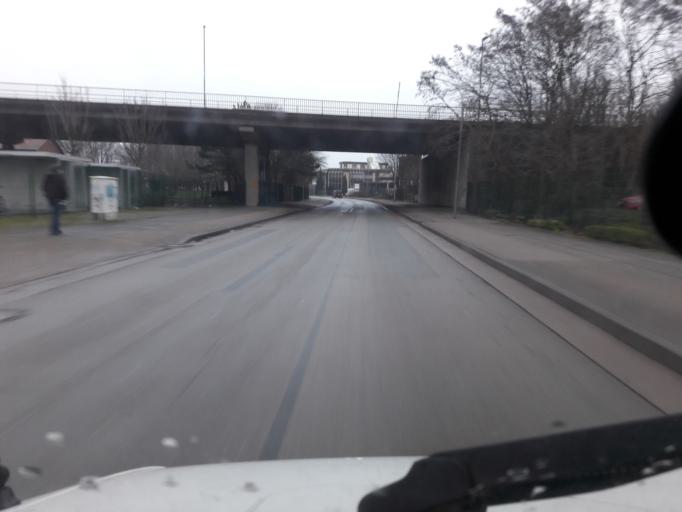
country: DE
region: North Rhine-Westphalia
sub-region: Regierungsbezirk Detmold
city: Minden
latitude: 52.2982
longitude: 8.9252
